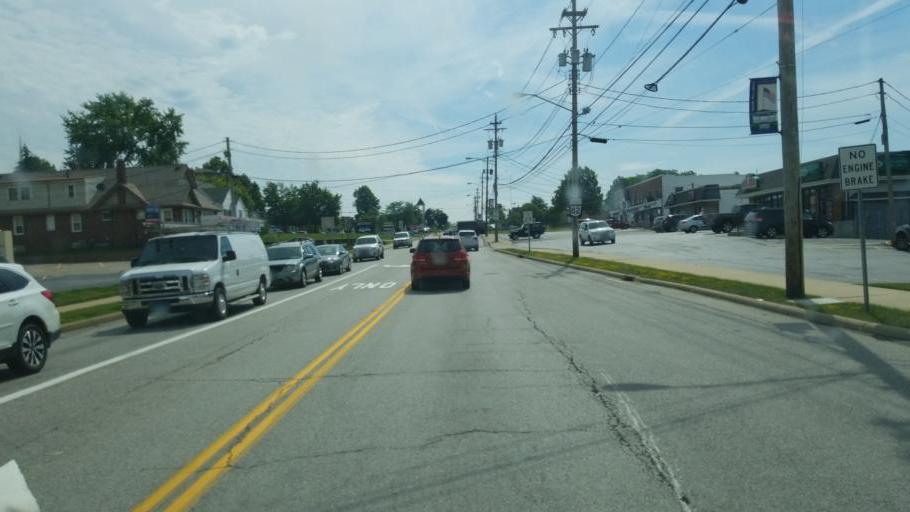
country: US
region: Ohio
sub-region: Cuyahoga County
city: North Royalton
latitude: 41.3137
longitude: -81.7346
